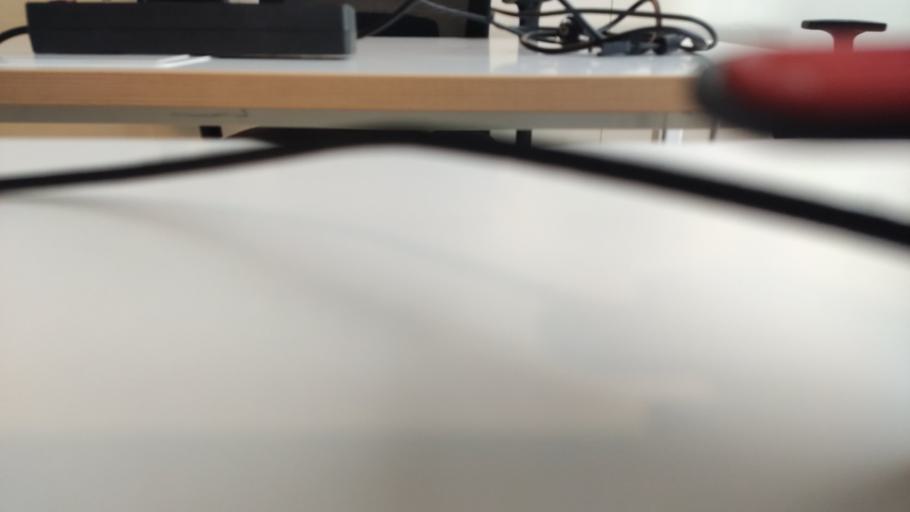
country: RU
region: Moskovskaya
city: Rogachevo
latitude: 56.4143
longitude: 37.0356
